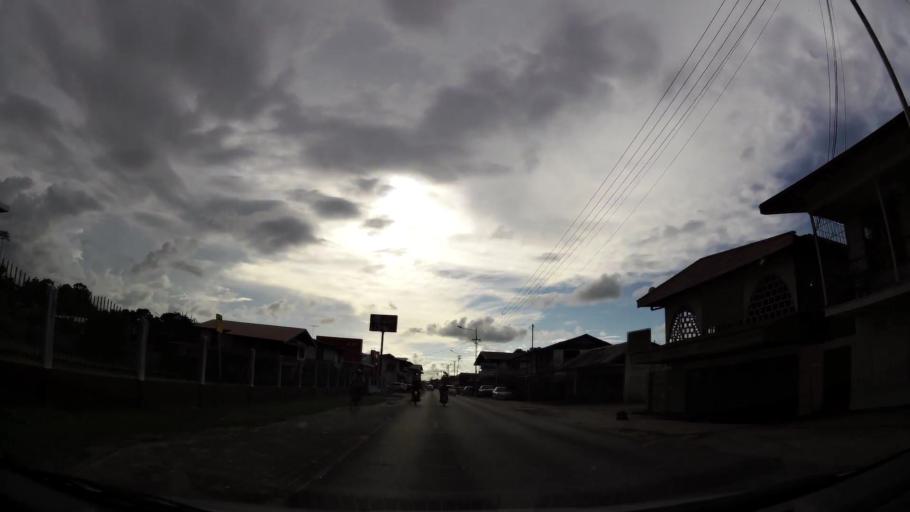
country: SR
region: Paramaribo
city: Paramaribo
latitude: 5.8368
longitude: -55.1733
